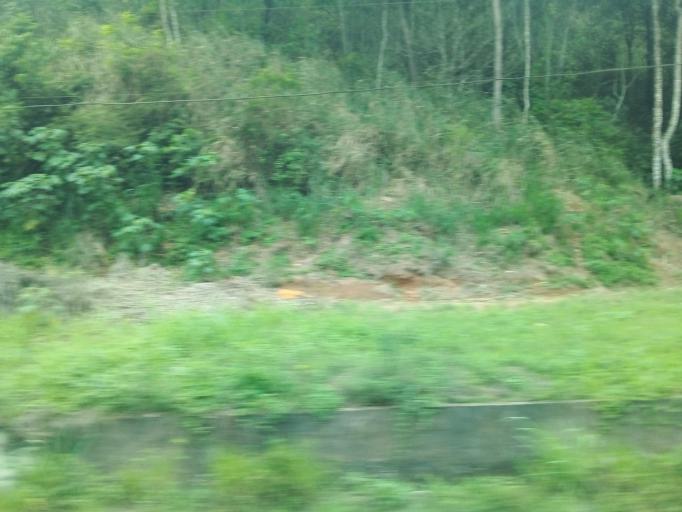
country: BR
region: Minas Gerais
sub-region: Nova Era
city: Nova Era
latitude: -19.7324
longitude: -43.0025
